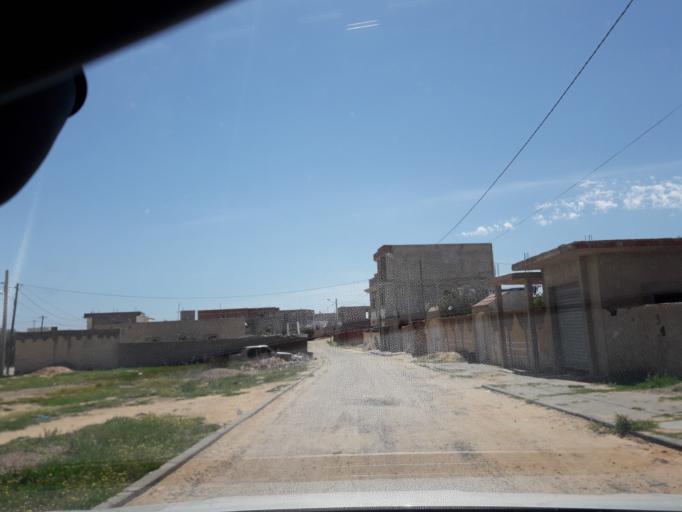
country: TN
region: Safaqis
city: Sfax
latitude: 34.7426
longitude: 10.5193
